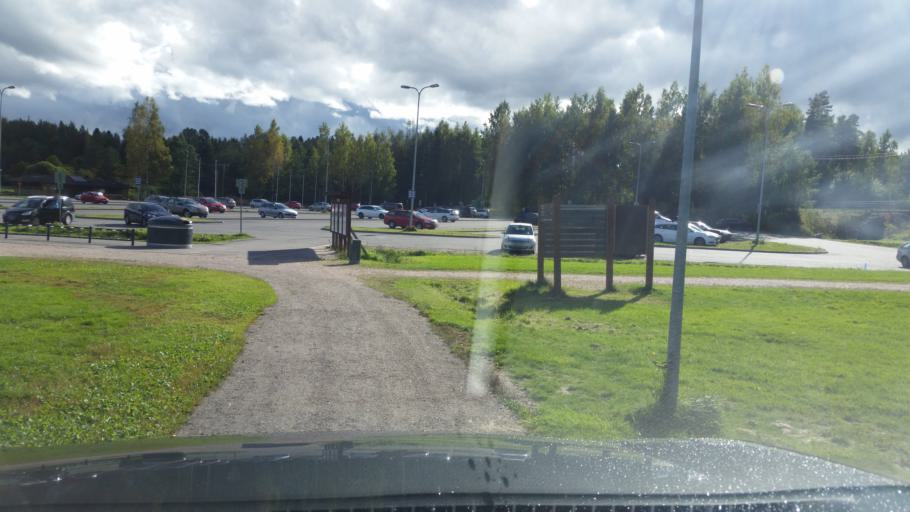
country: FI
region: Uusimaa
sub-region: Helsinki
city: Espoo
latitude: 60.2404
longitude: 24.6571
